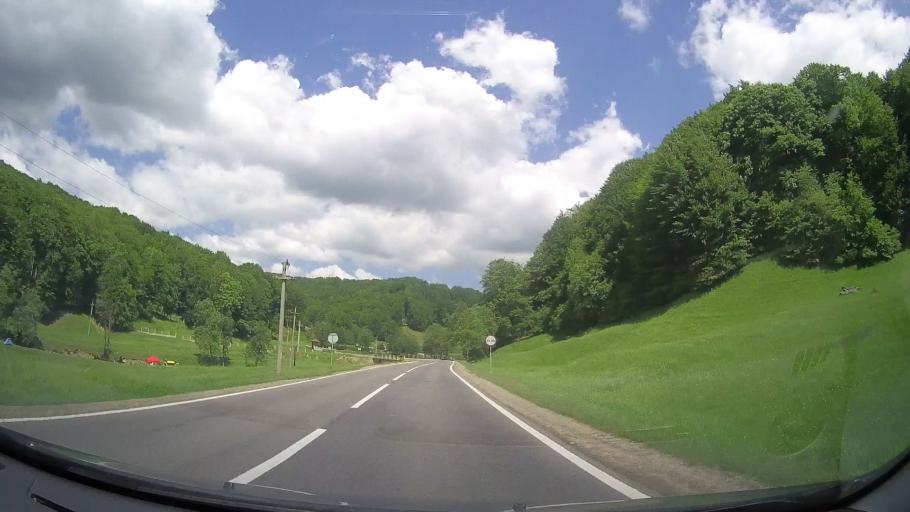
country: RO
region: Prahova
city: Maneciu
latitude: 45.4338
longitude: 25.9382
